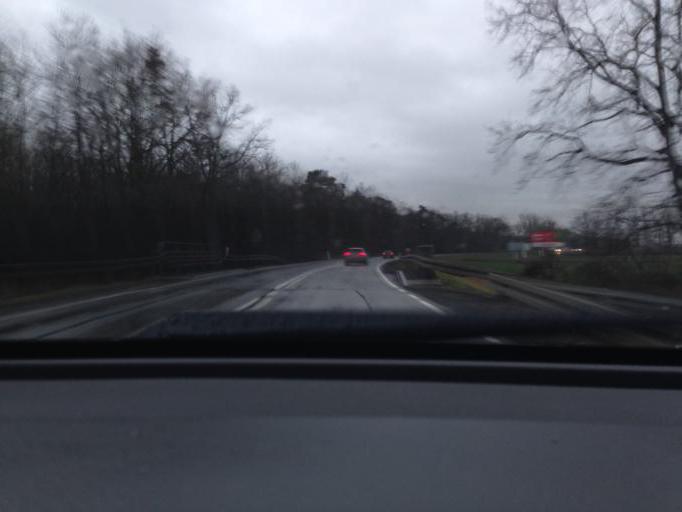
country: PL
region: Opole Voivodeship
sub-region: Powiat opolski
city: Wegry
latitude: 50.7073
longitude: 17.9845
